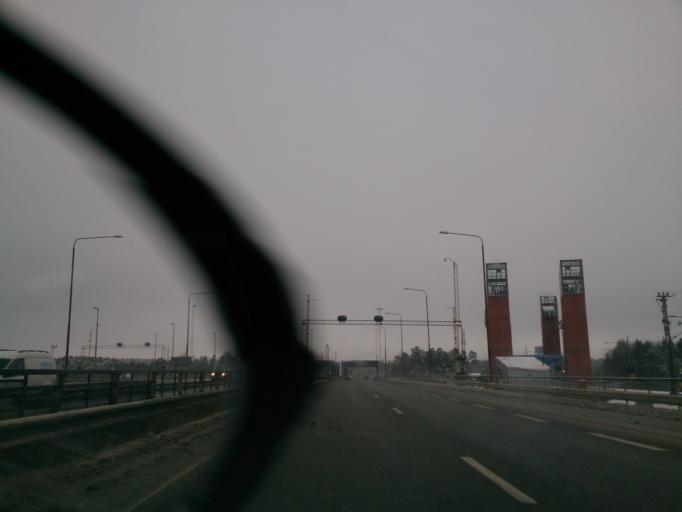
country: SE
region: Stockholm
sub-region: Sodertalje Kommun
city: Soedertaelje
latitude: 59.1830
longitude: 17.6423
